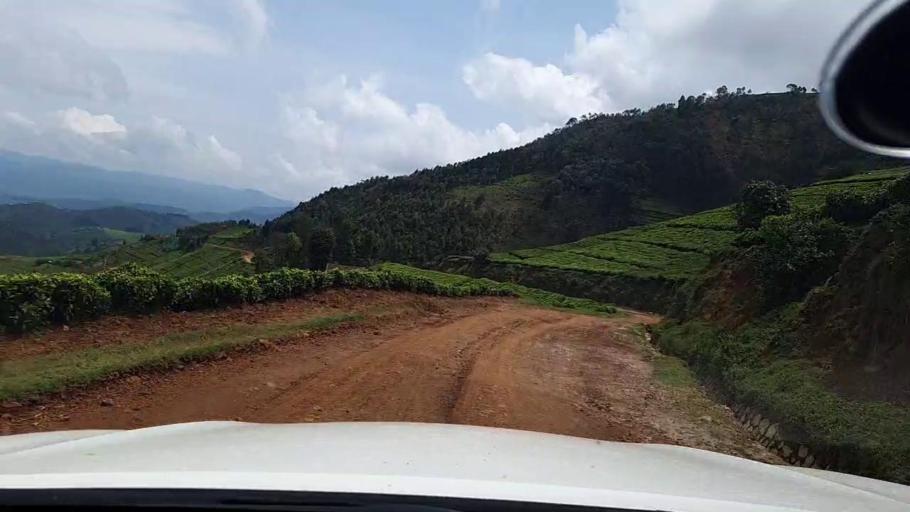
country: RW
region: Western Province
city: Kibuye
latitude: -2.1696
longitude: 29.3965
